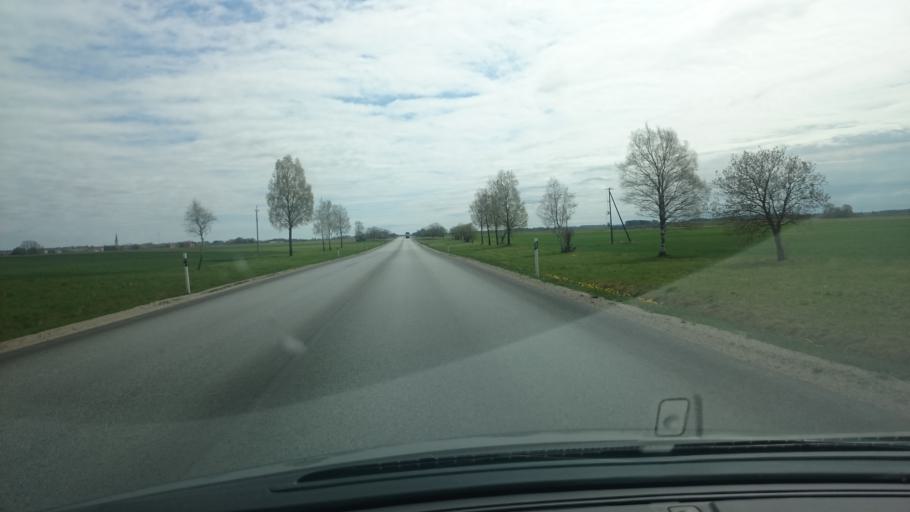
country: EE
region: Laeaene-Virumaa
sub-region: Haljala vald
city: Haljala
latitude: 59.4285
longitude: 26.2287
